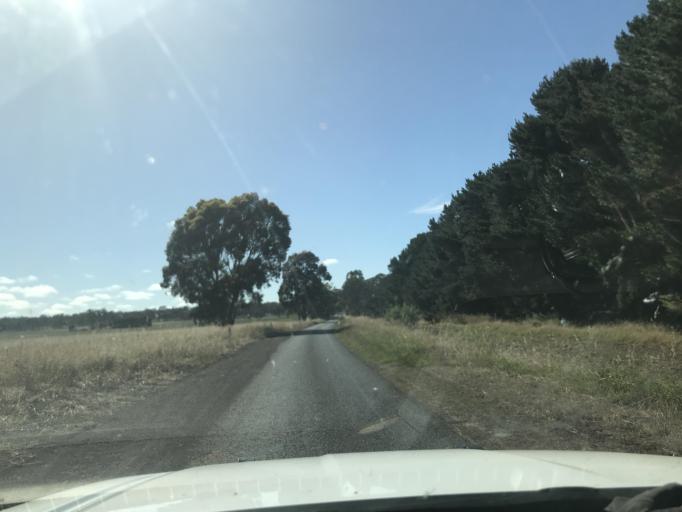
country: AU
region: Victoria
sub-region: Horsham
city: Horsham
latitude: -37.0881
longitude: 141.7611
